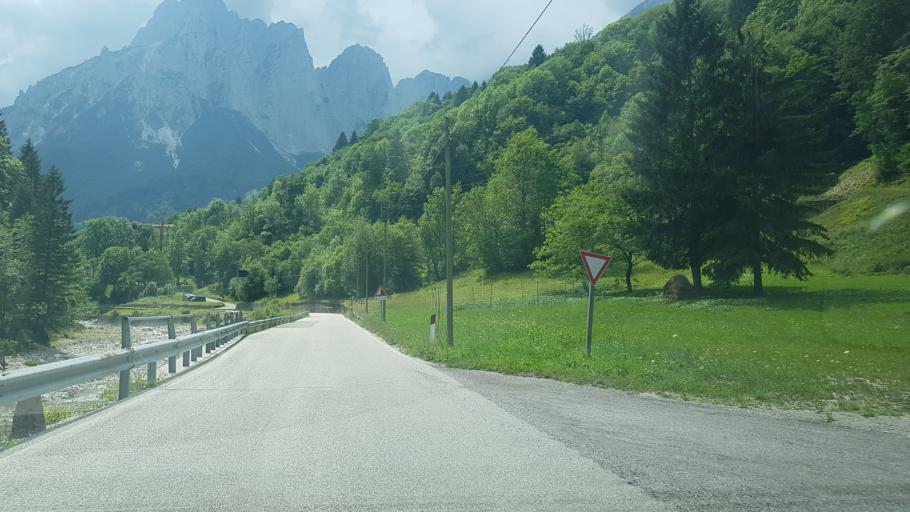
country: IT
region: Friuli Venezia Giulia
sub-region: Provincia di Udine
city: Moggio Udinese
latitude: 46.4894
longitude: 13.1968
